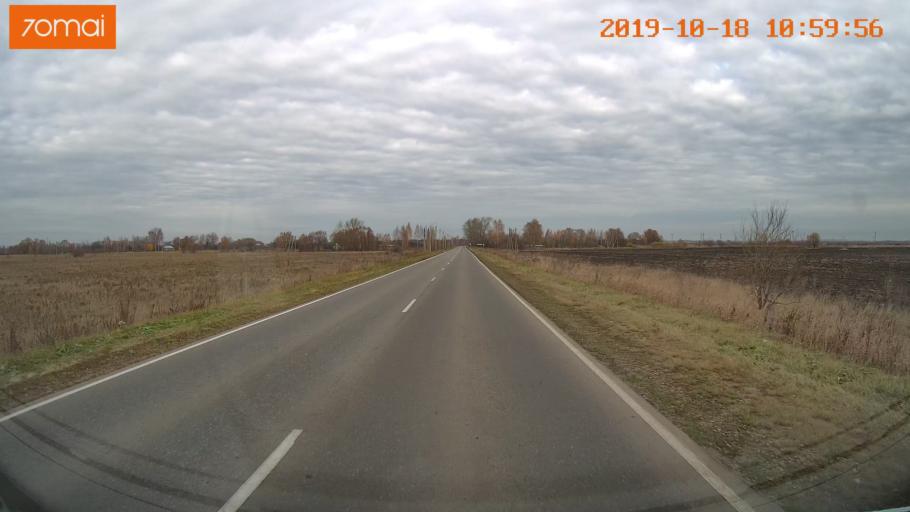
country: RU
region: Tula
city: Yepifan'
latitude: 53.8366
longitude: 38.5545
